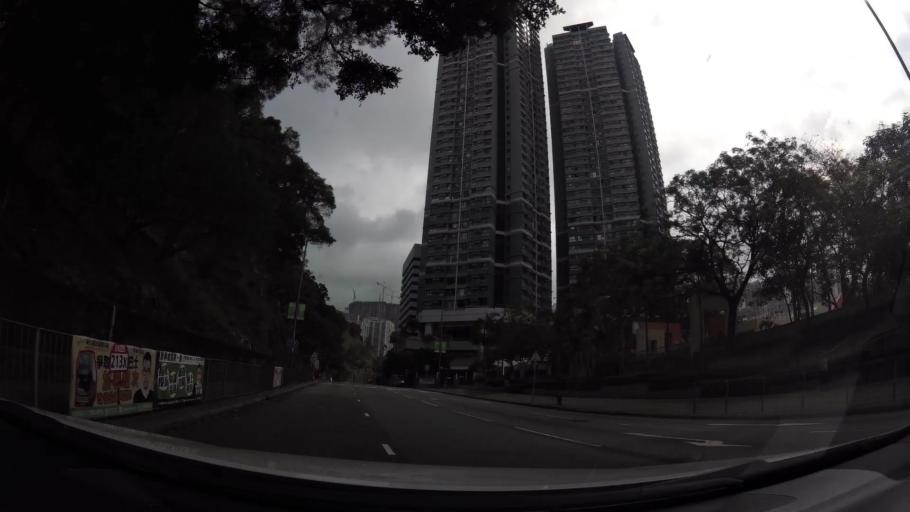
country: HK
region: Kowloon City
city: Kowloon
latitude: 22.3204
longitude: 114.2239
